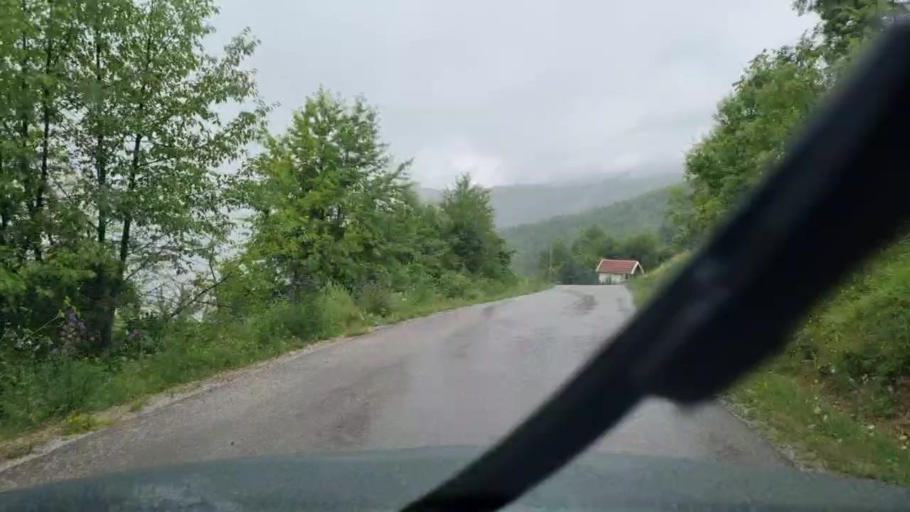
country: BA
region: Republika Srpska
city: Koran
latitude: 43.6390
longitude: 18.6193
